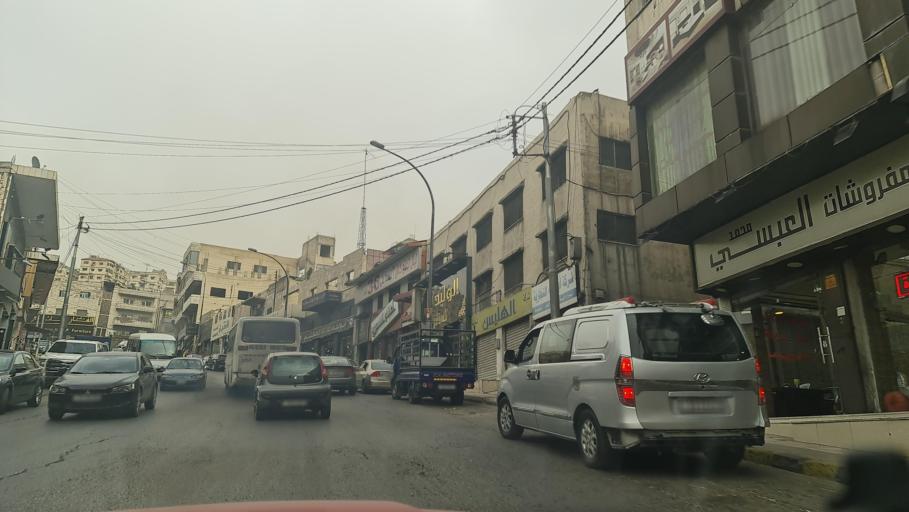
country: JO
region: Amman
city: Amman
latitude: 31.9379
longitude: 35.9296
